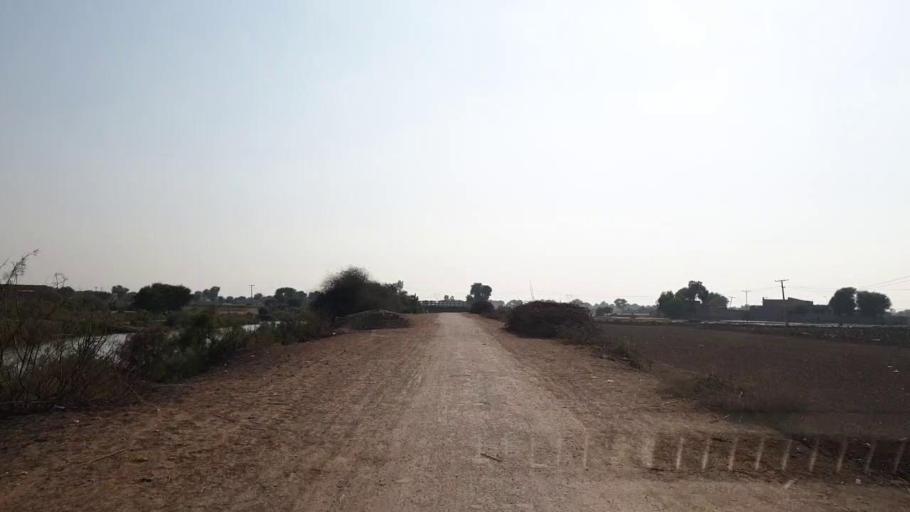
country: PK
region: Sindh
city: Sehwan
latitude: 26.4439
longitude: 67.8097
